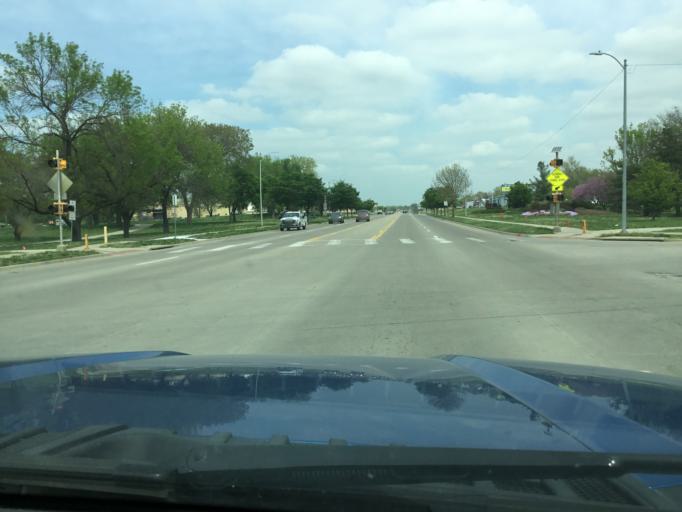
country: US
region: Kansas
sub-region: Shawnee County
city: Topeka
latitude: 39.0764
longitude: -95.6690
